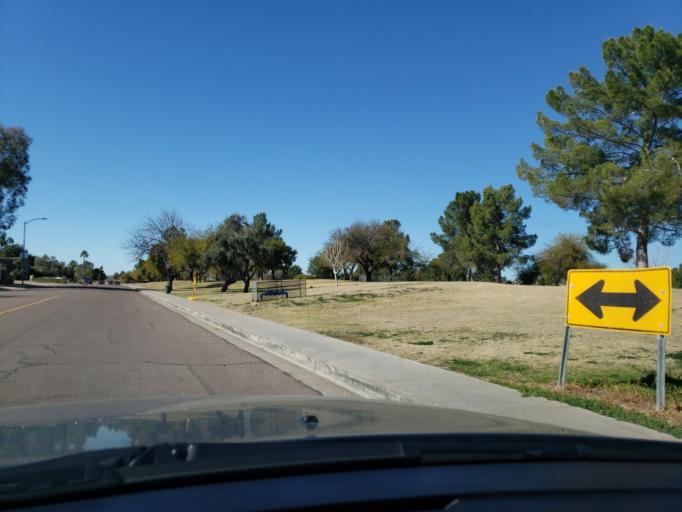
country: US
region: Arizona
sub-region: Maricopa County
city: Paradise Valley
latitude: 33.6150
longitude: -111.9366
